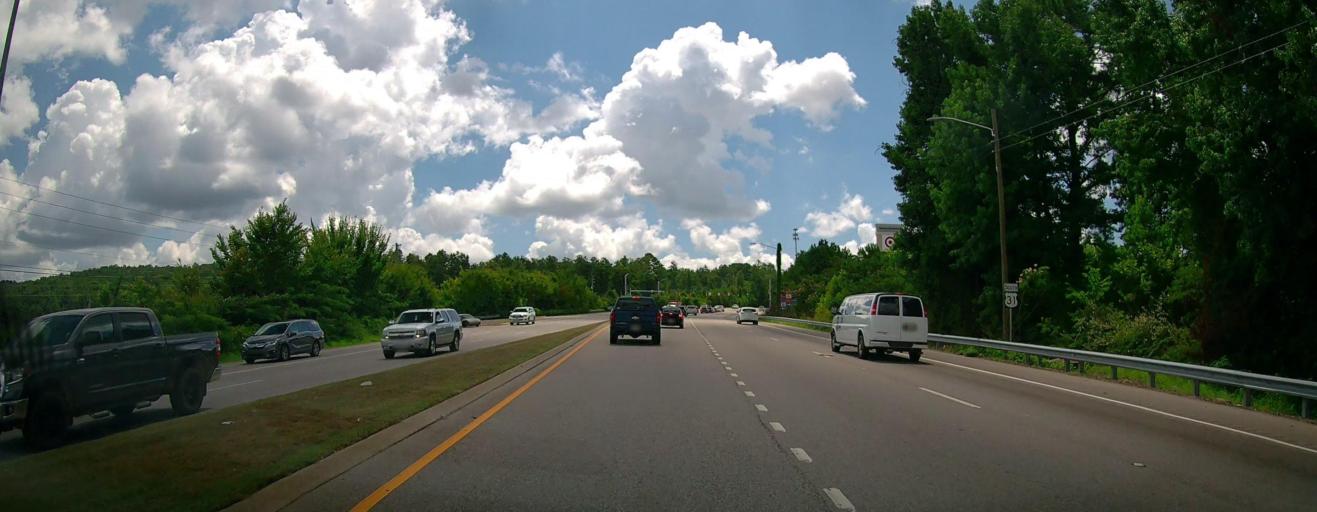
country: US
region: Alabama
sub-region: Shelby County
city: Alabaster
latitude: 33.2298
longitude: -86.8059
